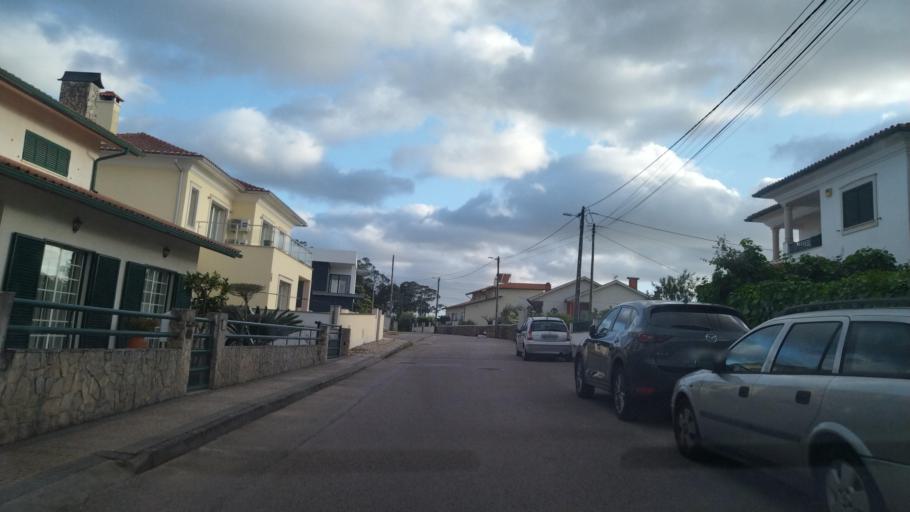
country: PT
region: Coimbra
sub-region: Coimbra
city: Coimbra
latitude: 40.1726
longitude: -8.4431
